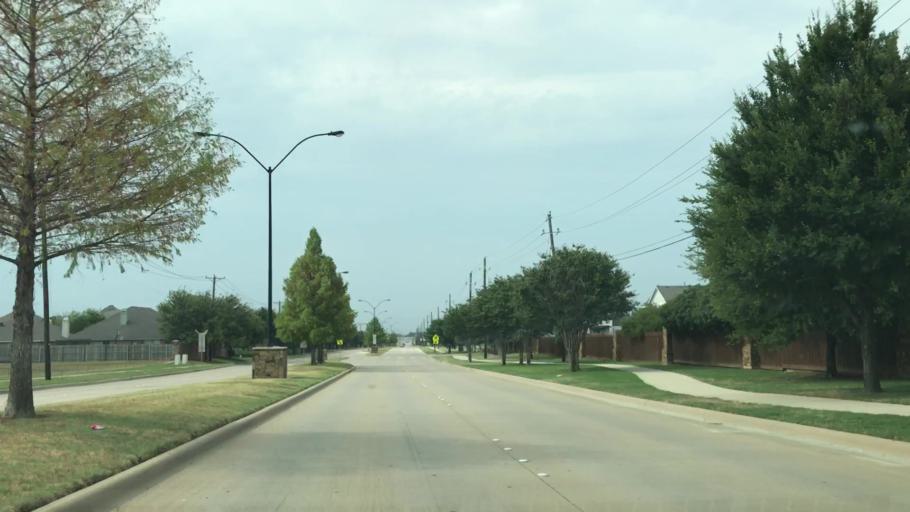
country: US
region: Texas
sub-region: Tarrant County
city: Keller
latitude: 32.9084
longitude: -97.2726
